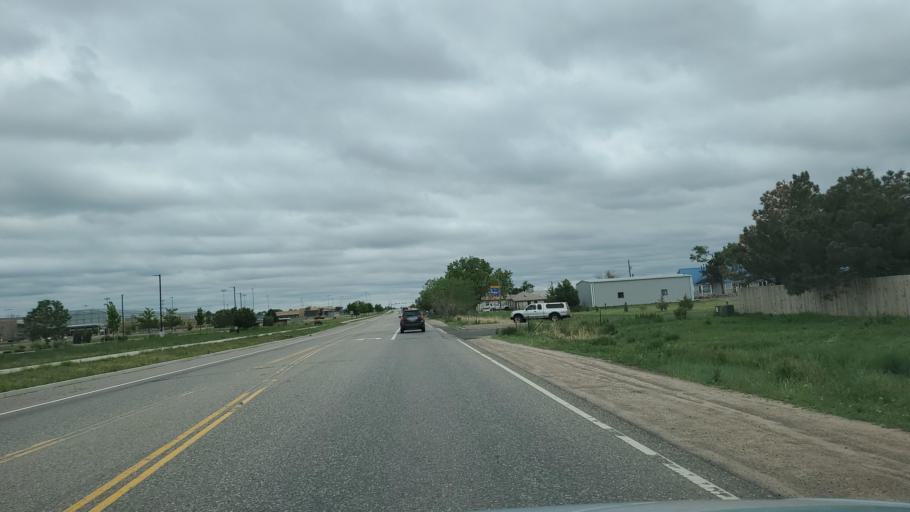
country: US
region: Colorado
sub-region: Adams County
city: Todd Creek
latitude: 39.9144
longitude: -104.8440
